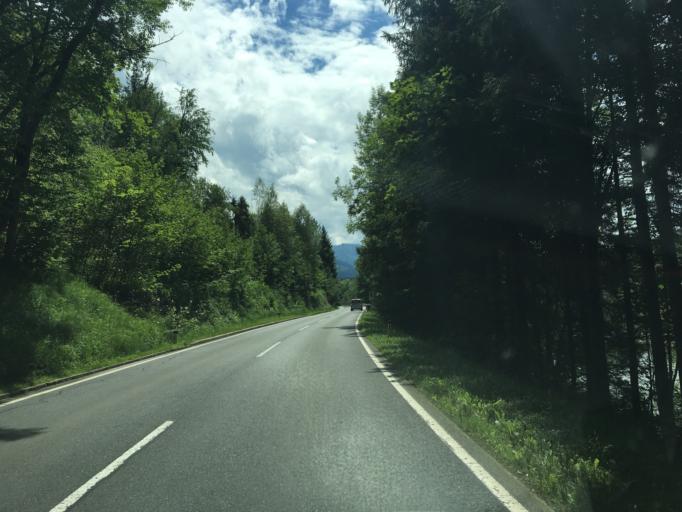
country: AT
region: Salzburg
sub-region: Politischer Bezirk Hallein
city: Adnet
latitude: 47.7148
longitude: 13.1359
